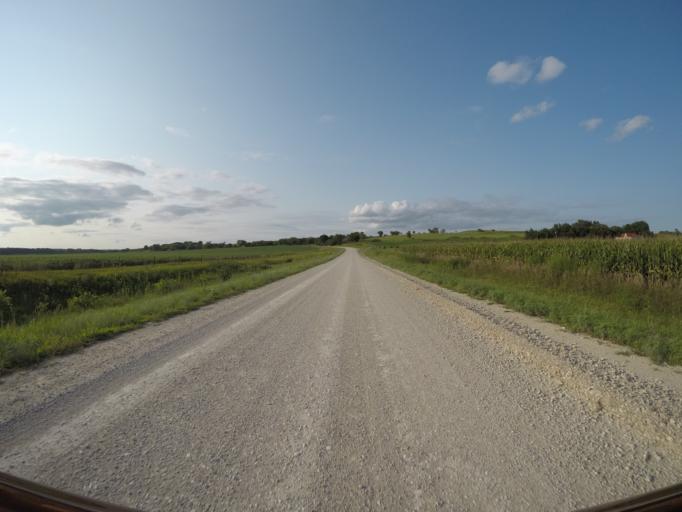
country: US
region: Kansas
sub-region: Wabaunsee County
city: Alma
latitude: 38.9600
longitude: -96.2520
